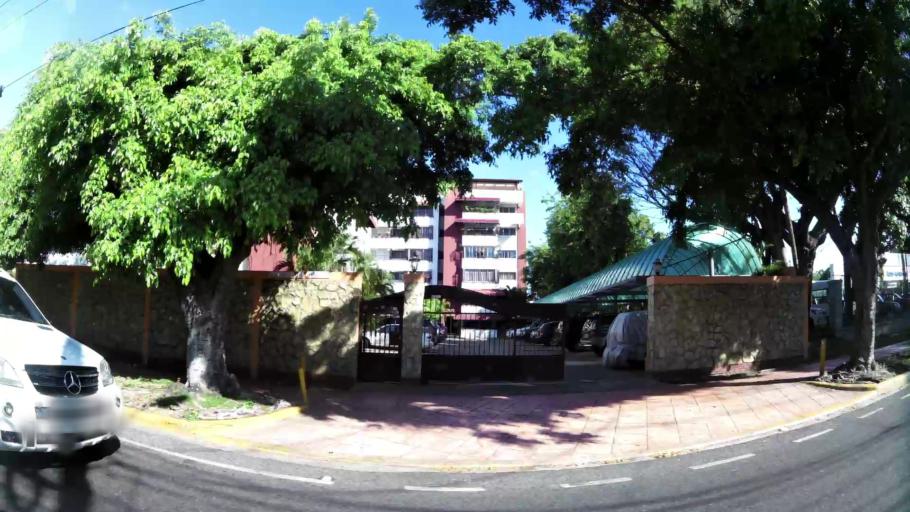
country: DO
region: Nacional
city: Ciudad Nueva
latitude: 18.4628
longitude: -69.9036
